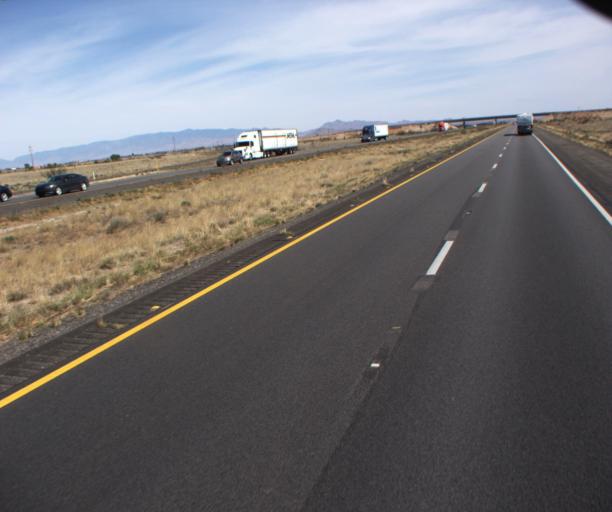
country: US
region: Arizona
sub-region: Cochise County
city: Willcox
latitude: 32.2187
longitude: -109.8808
